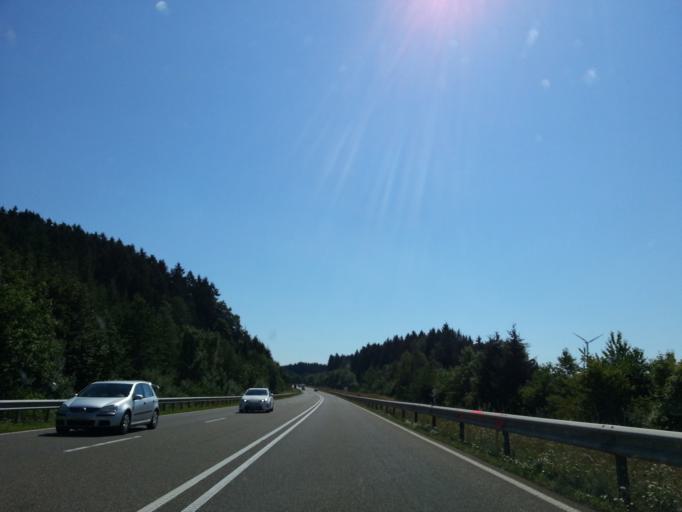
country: DE
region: Rheinland-Pfalz
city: Brandscheid
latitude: 50.2059
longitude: 6.3292
